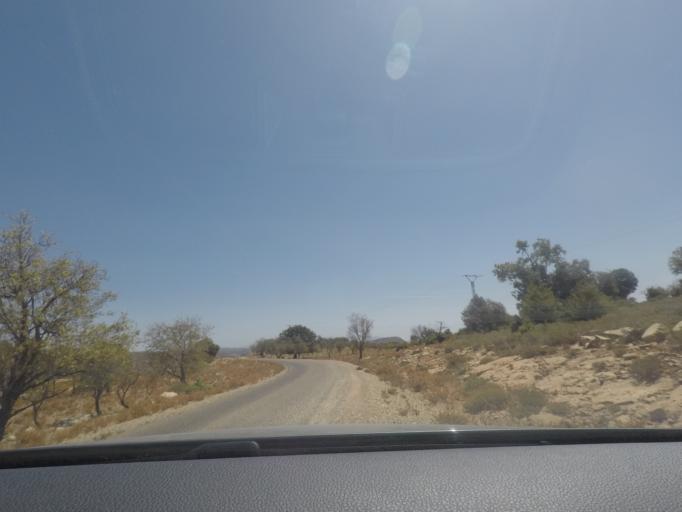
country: MA
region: Souss-Massa-Draa
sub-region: Agadir-Ida-ou-Tnan
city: Tadrart
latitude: 30.7369
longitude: -9.3680
